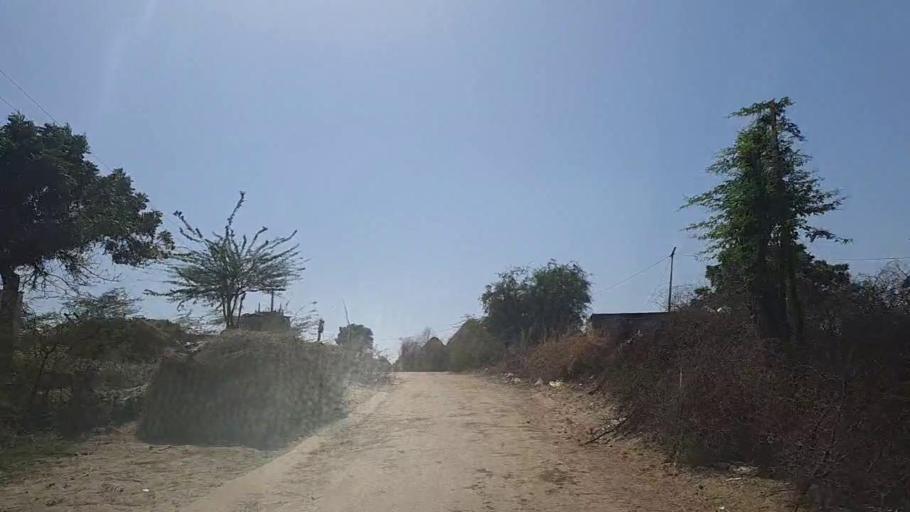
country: PK
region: Sindh
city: Mithi
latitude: 24.8359
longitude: 69.6500
